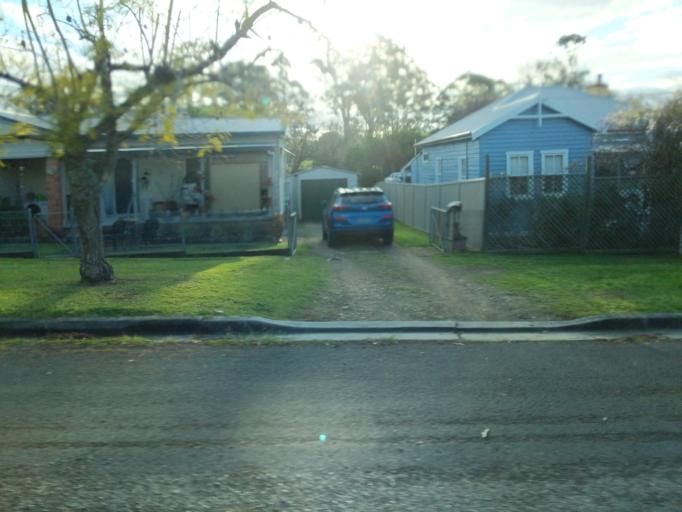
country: AU
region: New South Wales
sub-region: Dungog
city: Dungog
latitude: -32.4002
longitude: 151.7529
